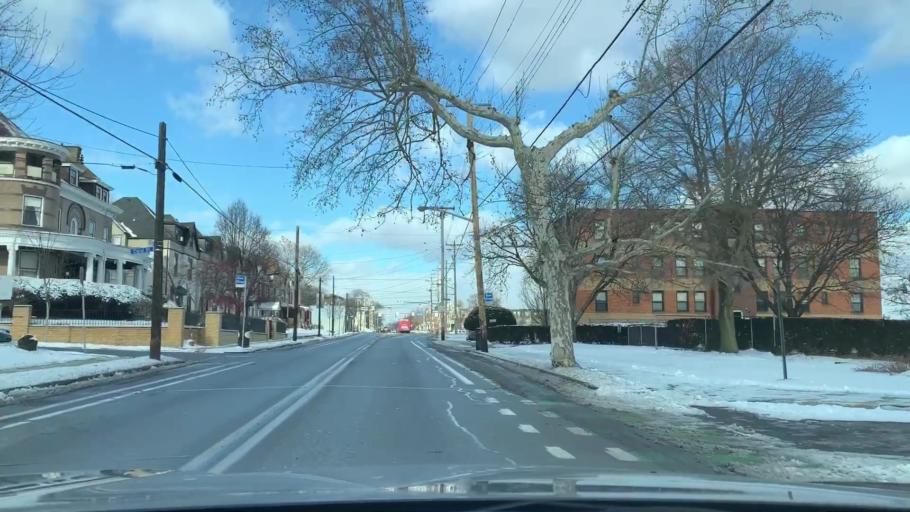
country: US
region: Pennsylvania
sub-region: Allegheny County
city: Bloomfield
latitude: 40.4617
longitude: -79.9317
